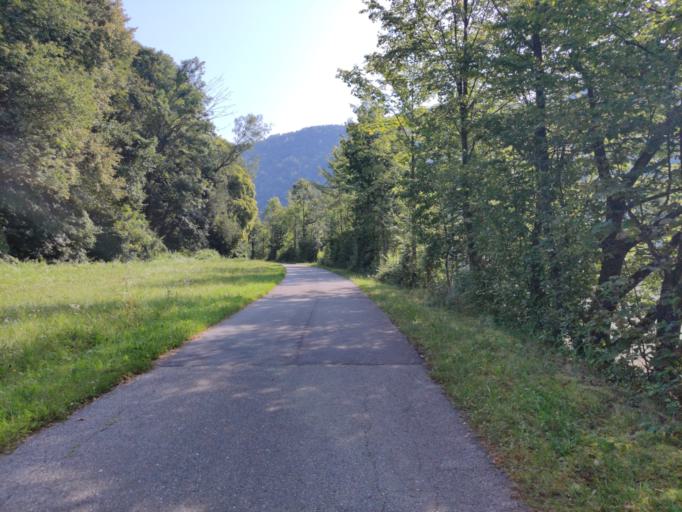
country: AT
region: Upper Austria
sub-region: Politischer Bezirk Rohrbach
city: Kleinzell im Muehlkreis
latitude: 48.4049
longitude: 13.9452
